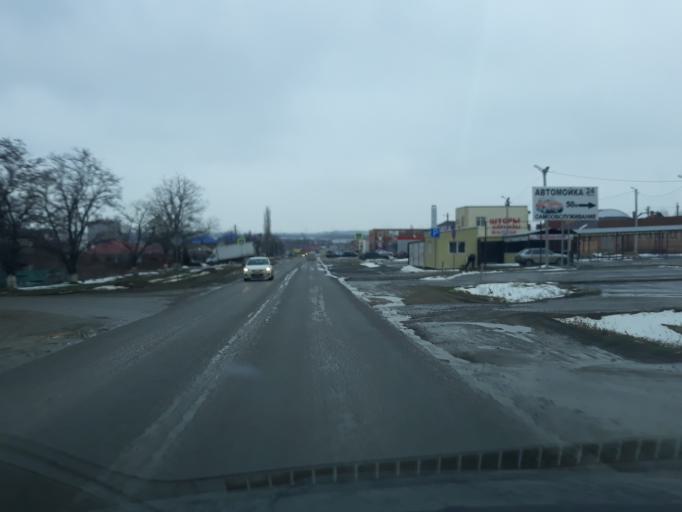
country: RU
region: Rostov
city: Krym
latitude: 47.2811
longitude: 39.5164
